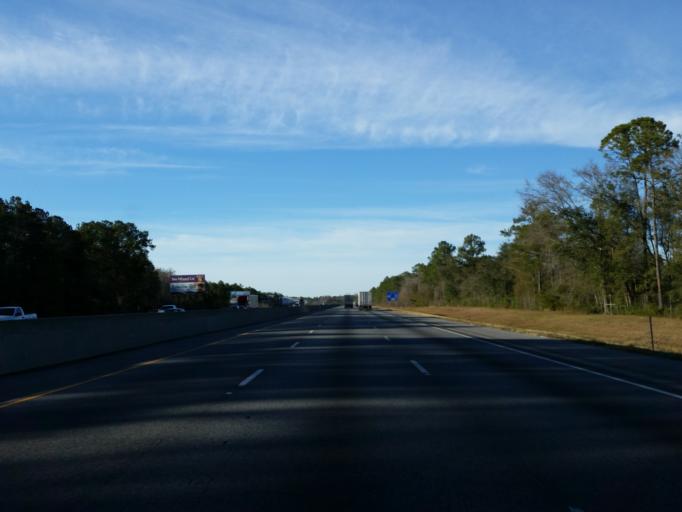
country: US
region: Georgia
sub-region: Lowndes County
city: Remerton
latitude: 30.8610
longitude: -83.3364
